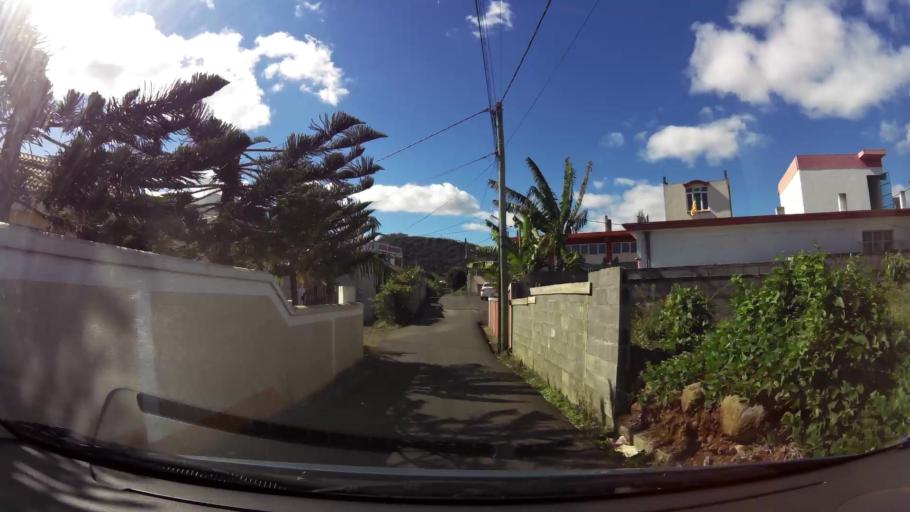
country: MU
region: Plaines Wilhems
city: Vacoas
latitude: -20.2834
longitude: 57.4772
